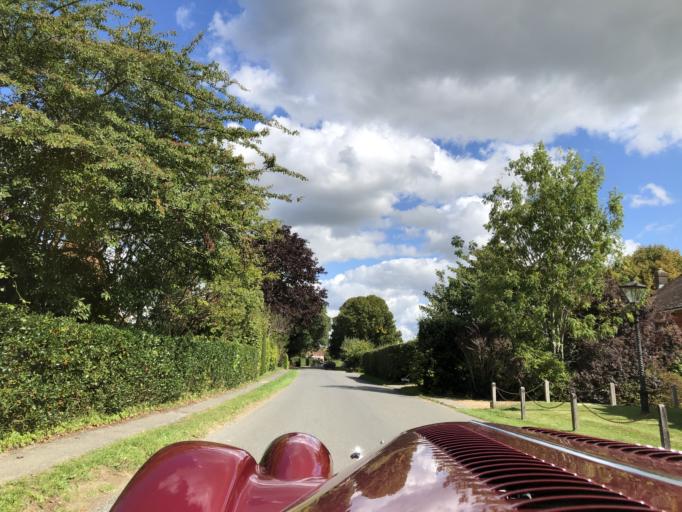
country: GB
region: England
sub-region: East Sussex
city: Northiam
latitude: 50.9918
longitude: 0.5542
